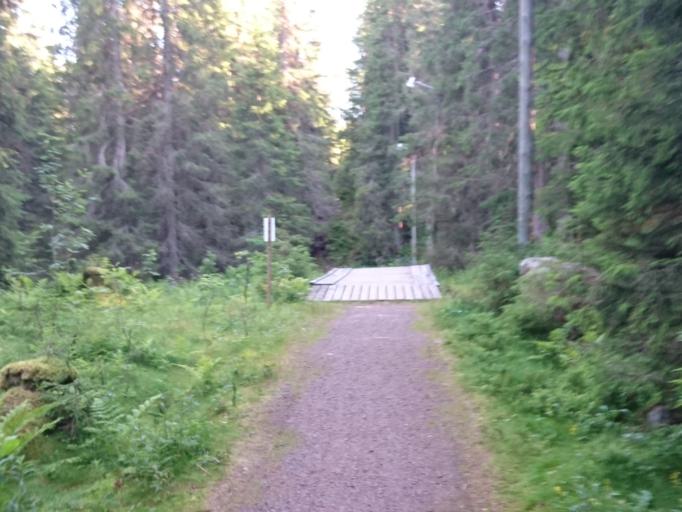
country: SE
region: Dalarna
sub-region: Malung-Saelens kommun
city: Malung
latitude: 61.1686
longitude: 13.1774
